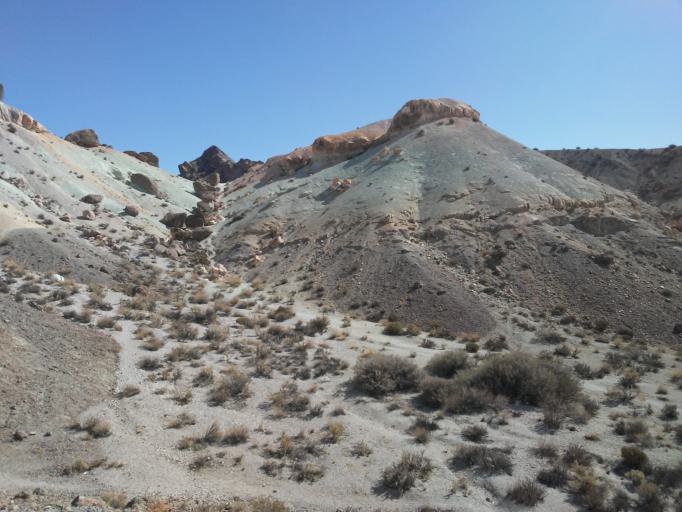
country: AR
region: Mendoza
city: Las Heras
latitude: -32.6195
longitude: -69.2661
